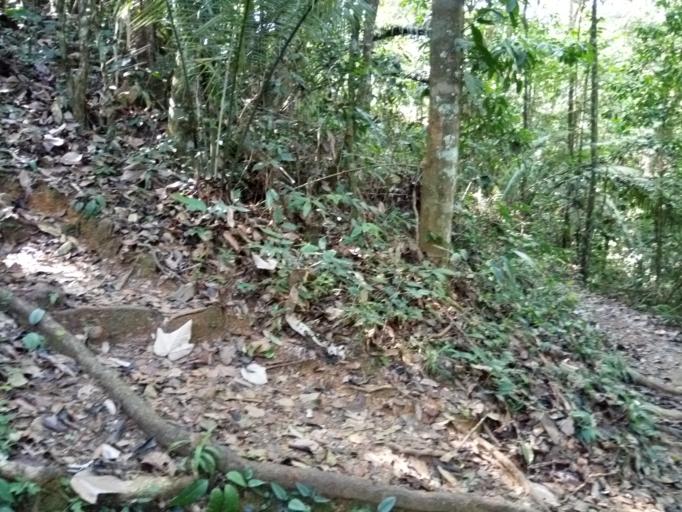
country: SR
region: Brokopondo
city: Brownsweg
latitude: 4.9540
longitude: -55.1897
